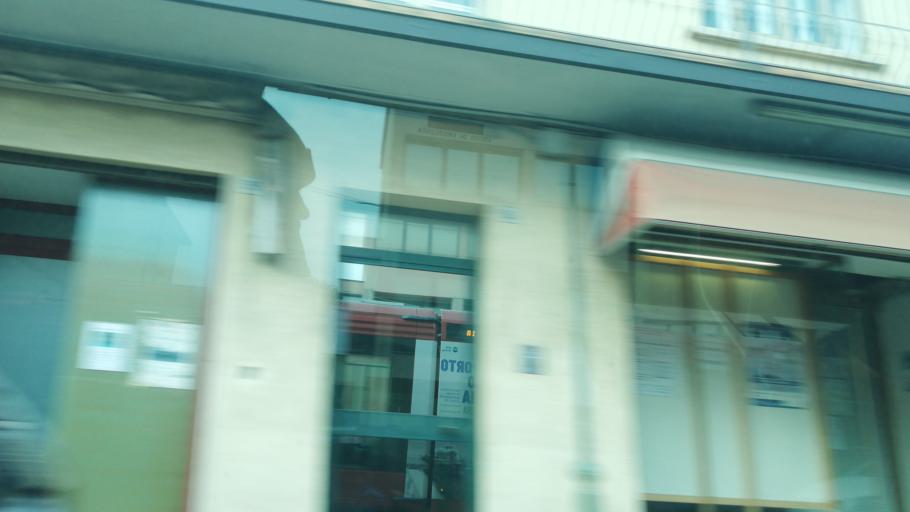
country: IT
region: Veneto
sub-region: Provincia di Venezia
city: Mestre
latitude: 45.4995
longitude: 12.2515
